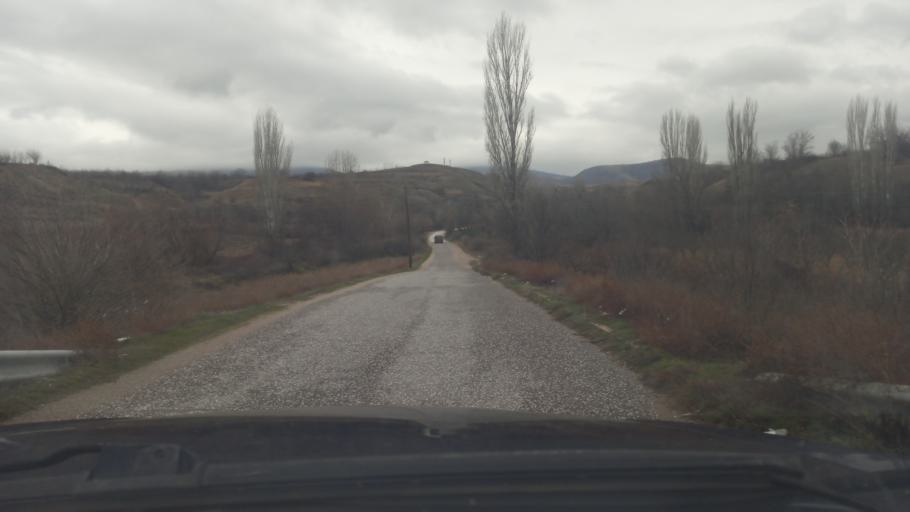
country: MK
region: Gradsko
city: Gradsko
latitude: 41.5999
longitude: 21.9104
